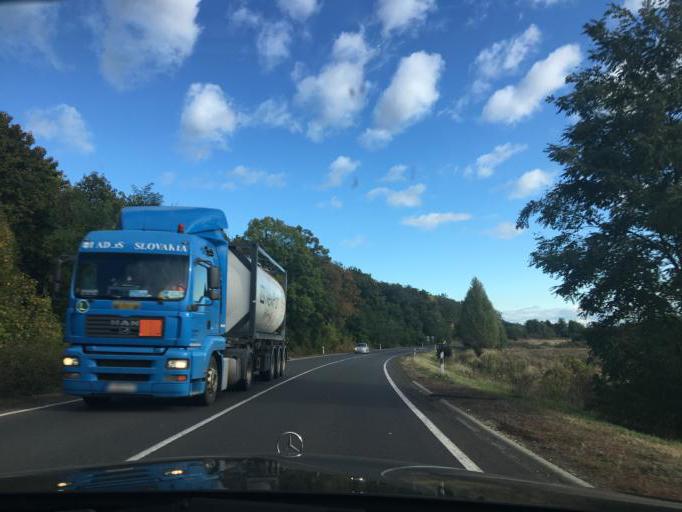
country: HU
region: Borsod-Abauj-Zemplen
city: Gonc
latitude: 48.4671
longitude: 21.1989
